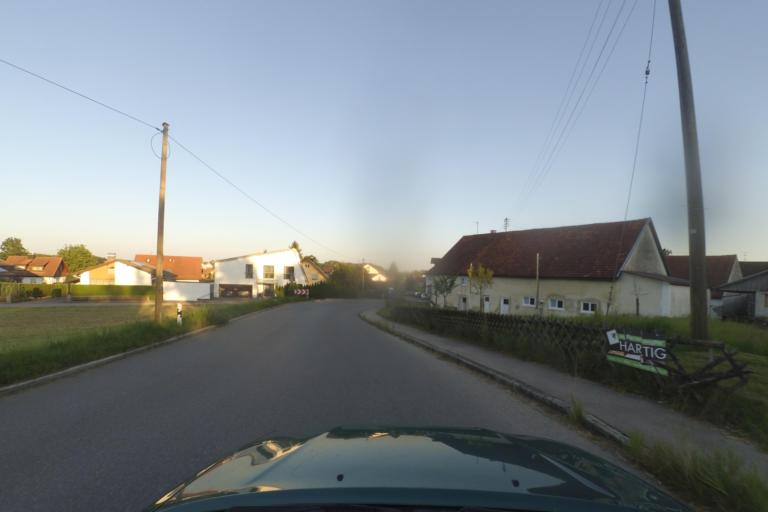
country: DE
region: Bavaria
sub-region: Upper Bavaria
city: Weil
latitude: 48.1021
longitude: 10.9065
